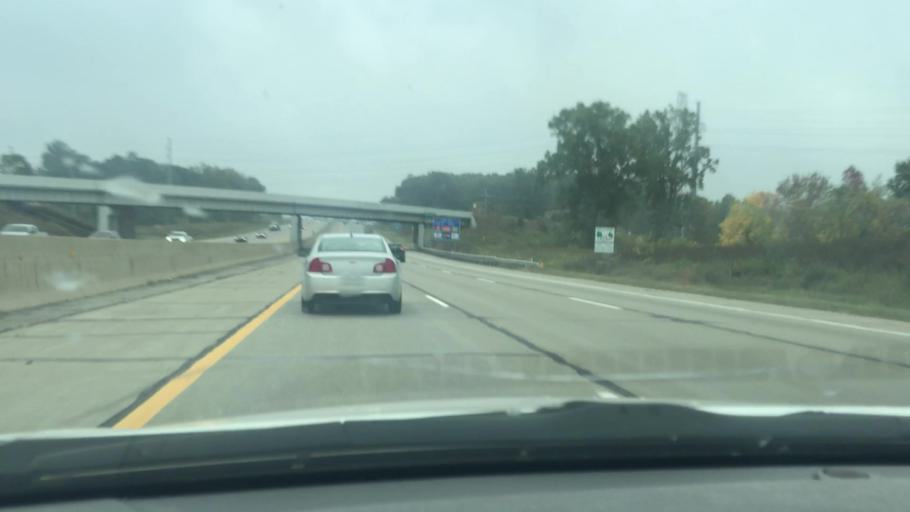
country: US
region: Michigan
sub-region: Livingston County
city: Howell
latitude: 42.5823
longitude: -83.8986
